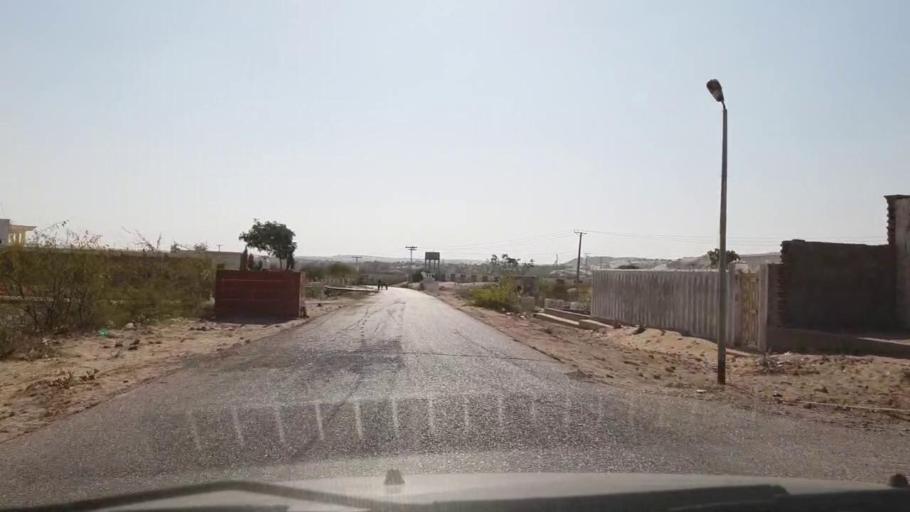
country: PK
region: Sindh
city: Diplo
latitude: 24.4800
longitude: 69.5811
